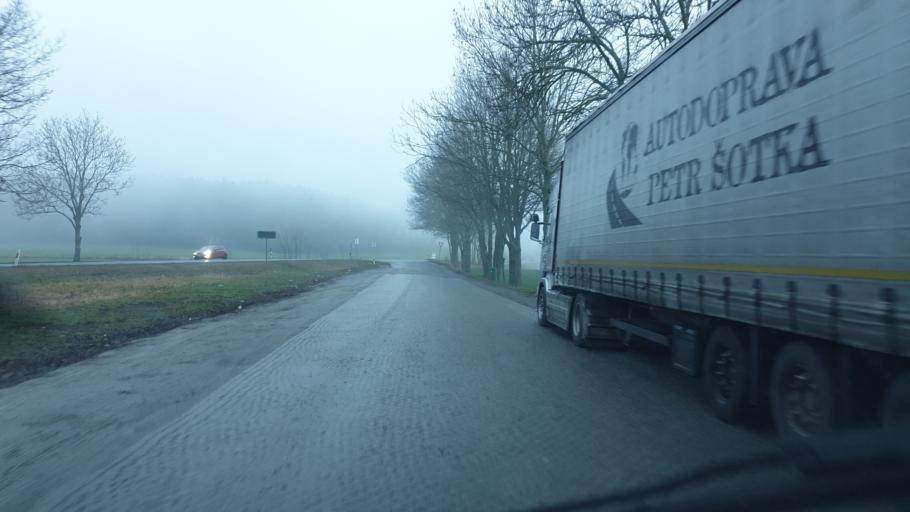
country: DE
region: Saxony
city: Grossolbersdorf
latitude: 50.6993
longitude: 13.1100
